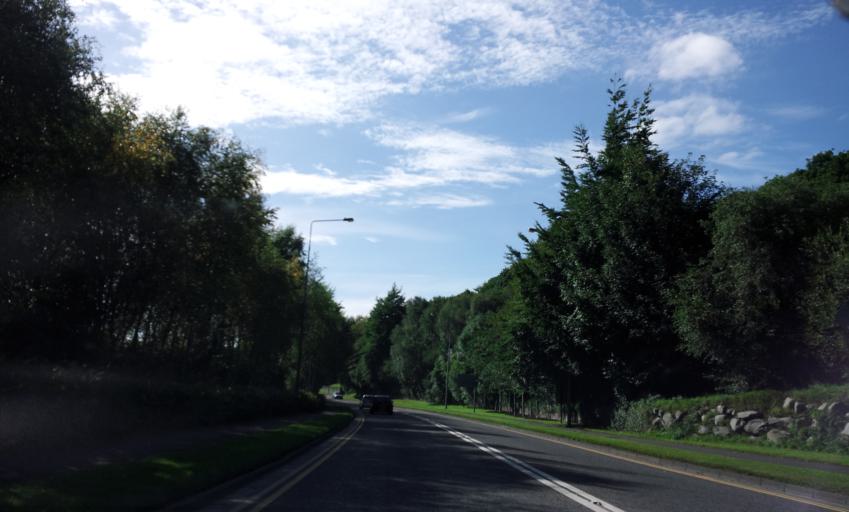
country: IE
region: Munster
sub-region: Ciarrai
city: Cill Airne
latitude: 52.0583
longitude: -9.4737
